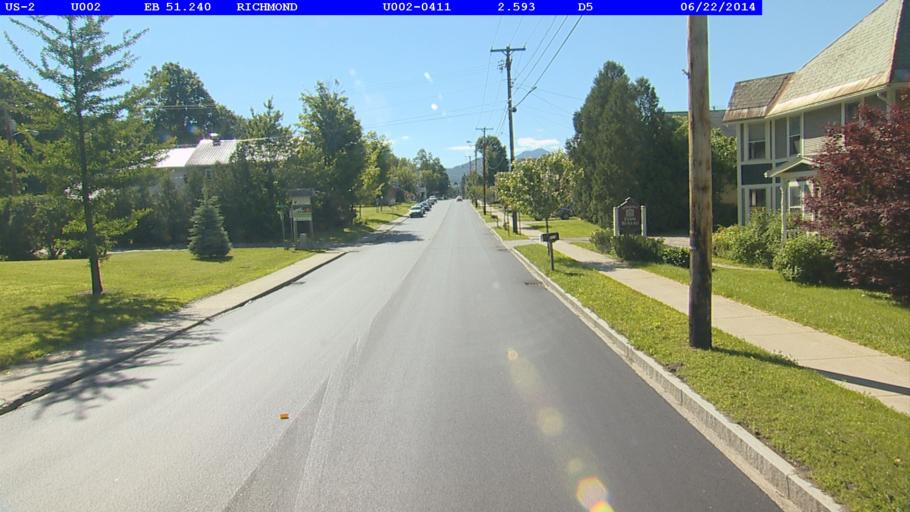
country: US
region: Vermont
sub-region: Chittenden County
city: Williston
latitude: 44.4064
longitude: -72.9949
